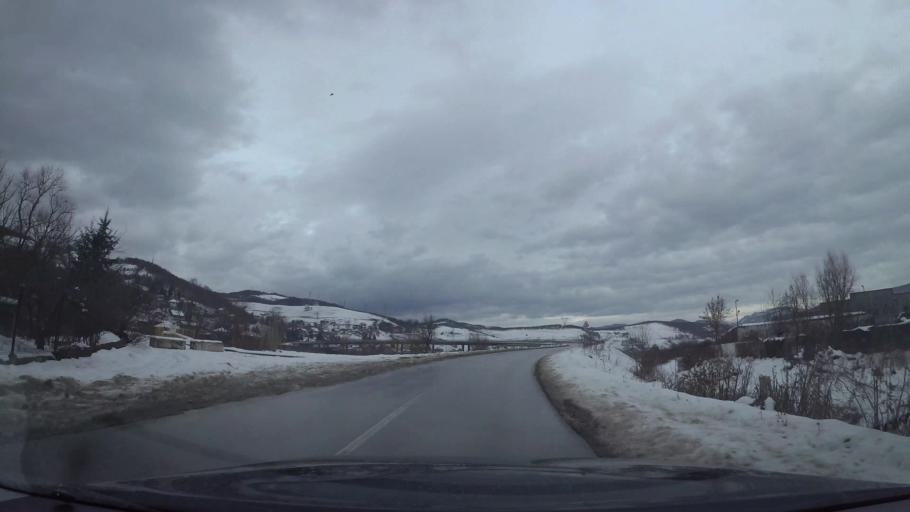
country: BA
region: Federation of Bosnia and Herzegovina
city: Vogosca
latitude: 43.8814
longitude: 18.3056
